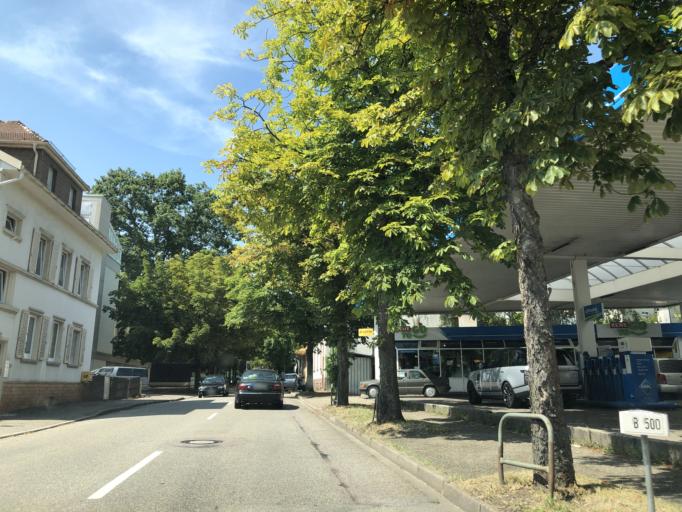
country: DE
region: Baden-Wuerttemberg
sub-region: Karlsruhe Region
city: Baden-Baden
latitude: 48.7493
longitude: 8.2547
